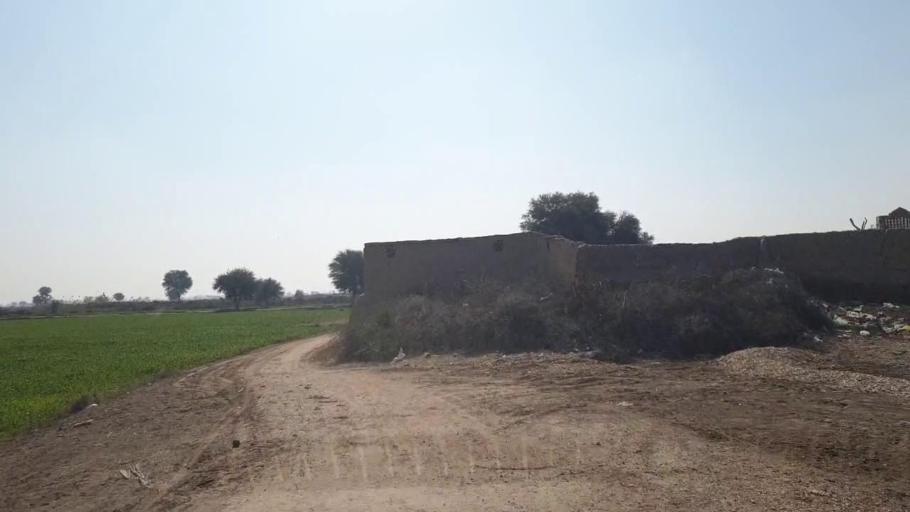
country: PK
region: Sindh
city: Shahpur Chakar
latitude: 26.1176
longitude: 68.6057
